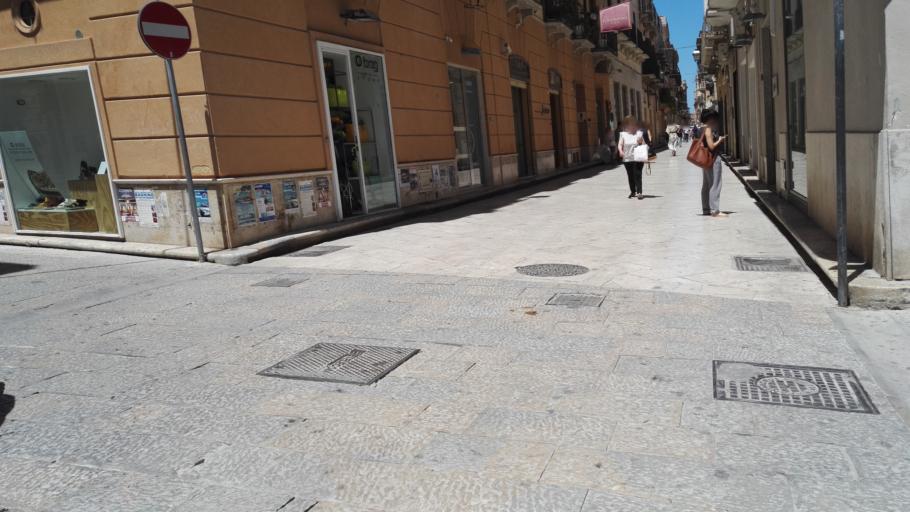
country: IT
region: Sicily
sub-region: Trapani
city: Marsala
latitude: 37.7981
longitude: 12.4371
